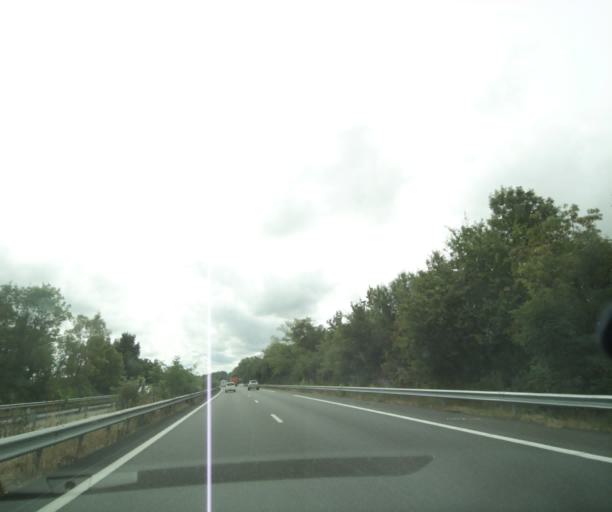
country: FR
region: Poitou-Charentes
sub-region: Departement de la Charente-Maritime
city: Mirambeau
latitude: 45.3818
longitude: -0.6018
